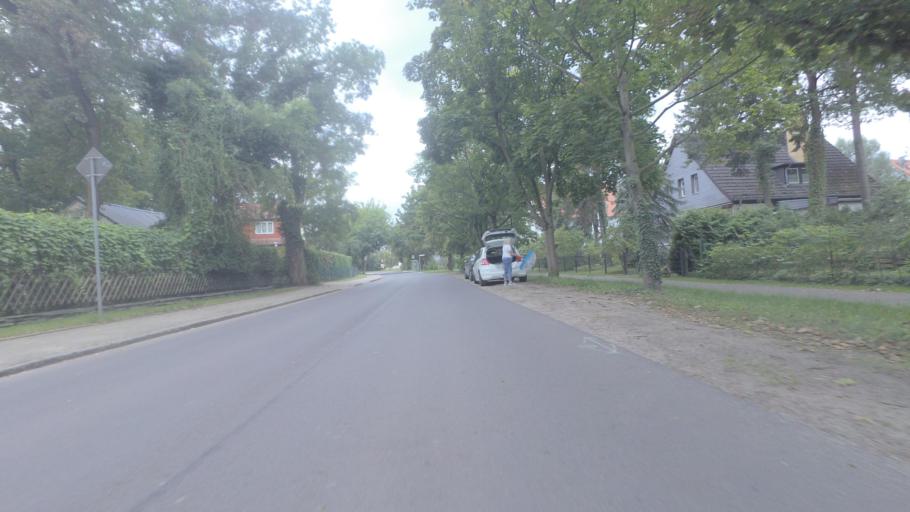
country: DE
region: Brandenburg
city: Potsdam
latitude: 52.3453
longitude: 13.1030
